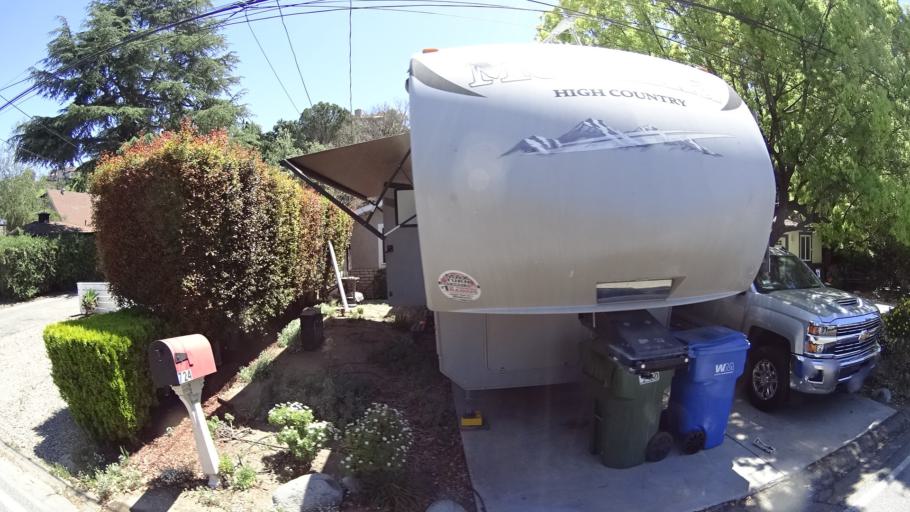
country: US
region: California
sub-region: Ventura County
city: Thousand Oaks
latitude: 34.1871
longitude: -118.8651
